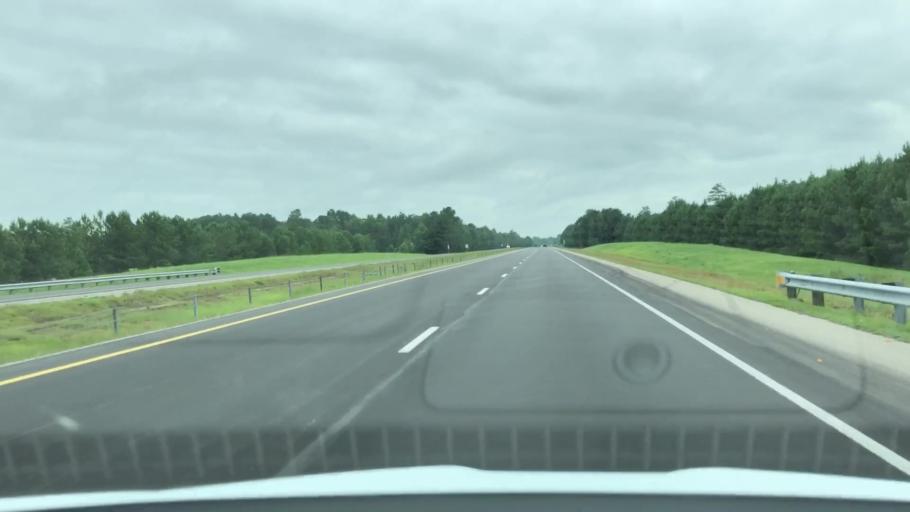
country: US
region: North Carolina
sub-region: Wilson County
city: Lucama
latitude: 35.6073
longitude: -77.9801
